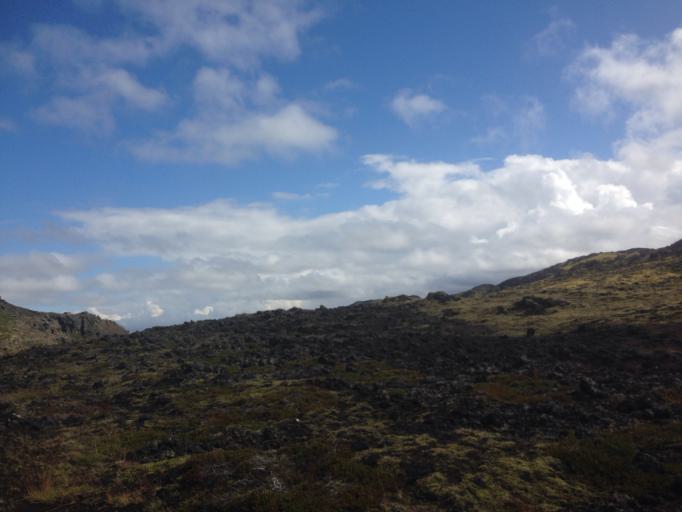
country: IS
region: Capital Region
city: Alftanes
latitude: 63.9518
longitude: -22.0845
